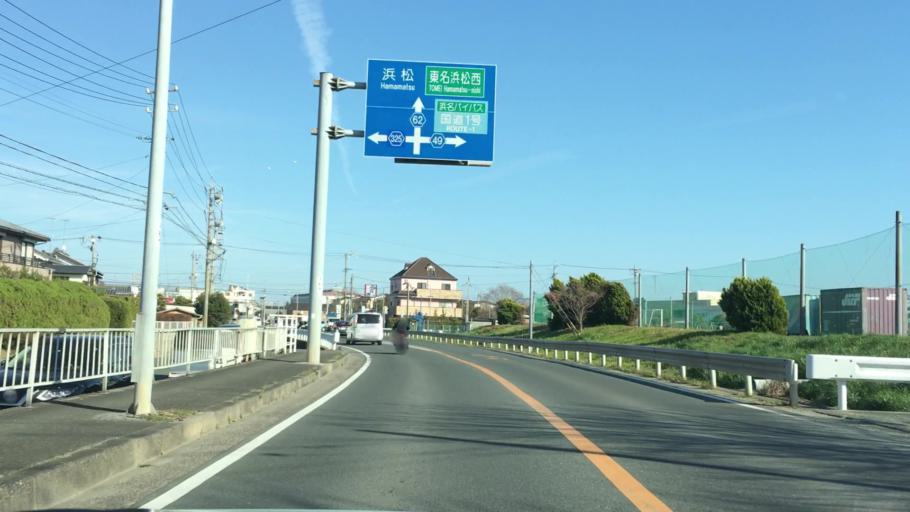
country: JP
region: Shizuoka
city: Kosai-shi
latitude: 34.6959
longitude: 137.6285
